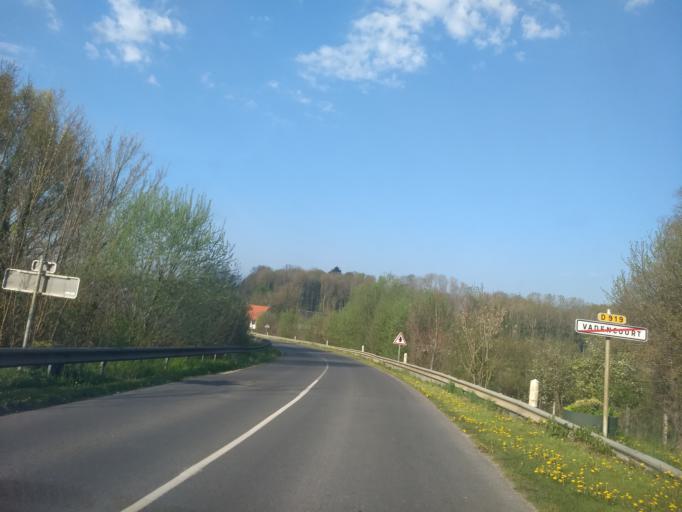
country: FR
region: Picardie
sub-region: Departement de la Somme
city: Corbie
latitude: 50.0080
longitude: 2.4855
